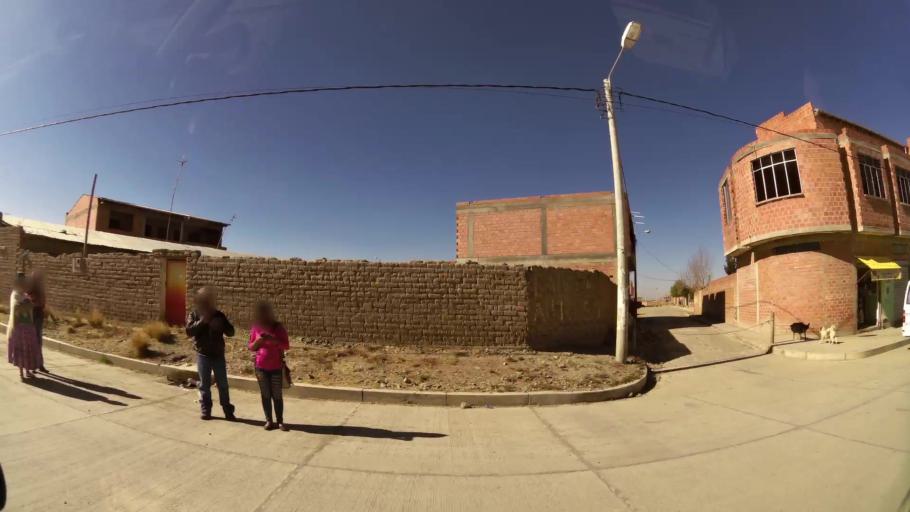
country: BO
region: La Paz
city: La Paz
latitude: -16.5309
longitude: -68.2343
